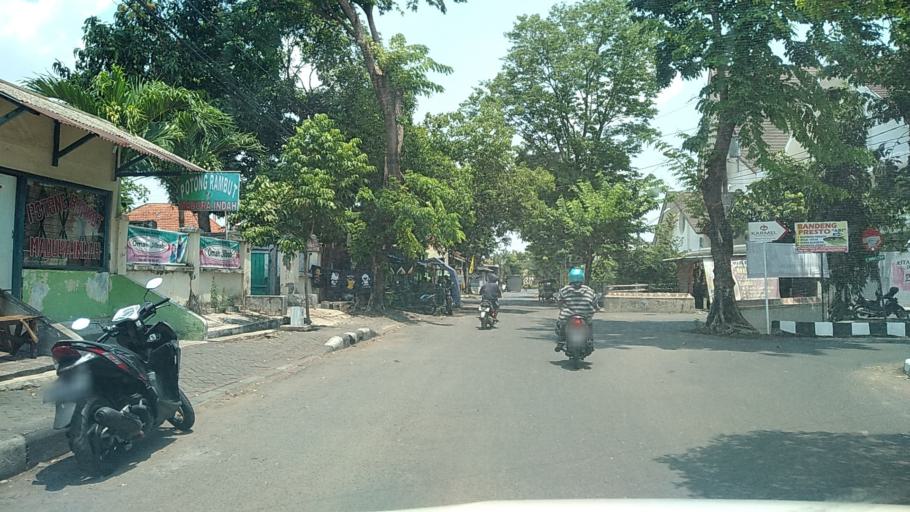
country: ID
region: Central Java
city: Semarang
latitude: -7.0065
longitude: 110.4391
